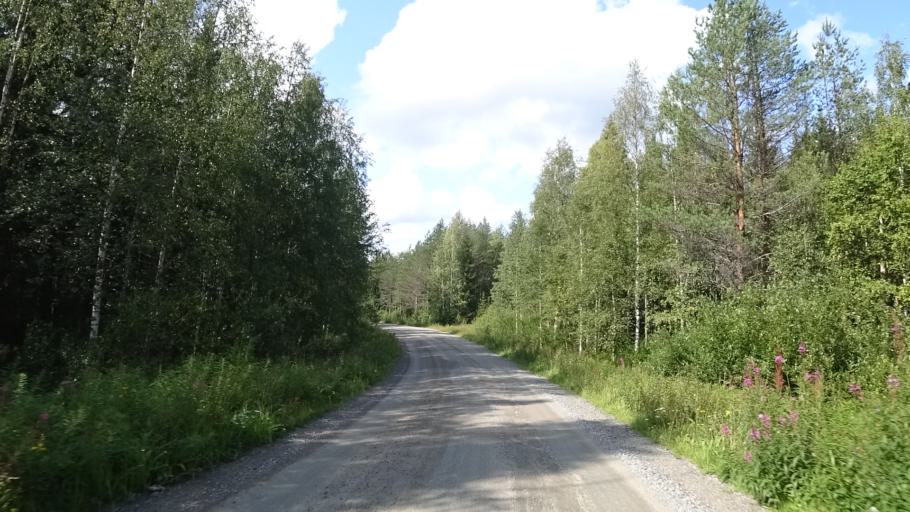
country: FI
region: North Karelia
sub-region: Joensuu
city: Ilomantsi
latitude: 62.9333
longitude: 31.3063
